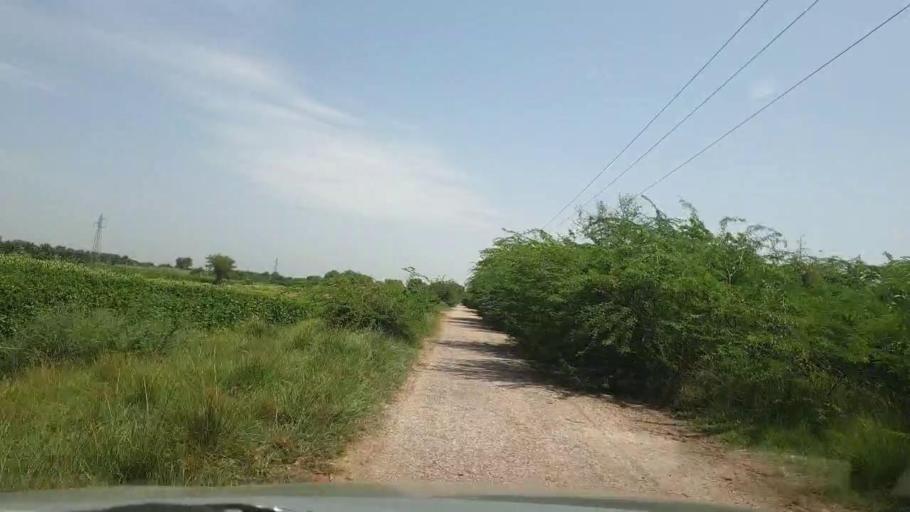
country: PK
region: Sindh
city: Bozdar
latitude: 27.1054
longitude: 68.9801
